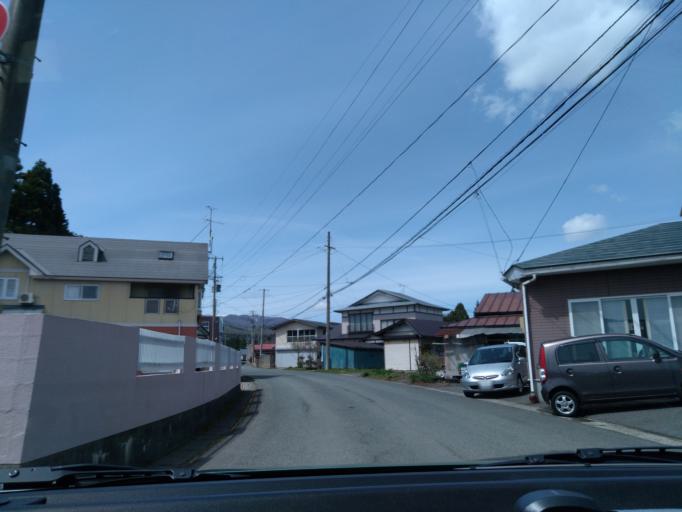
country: JP
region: Iwate
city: Kitakami
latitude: 39.3054
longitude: 140.9746
